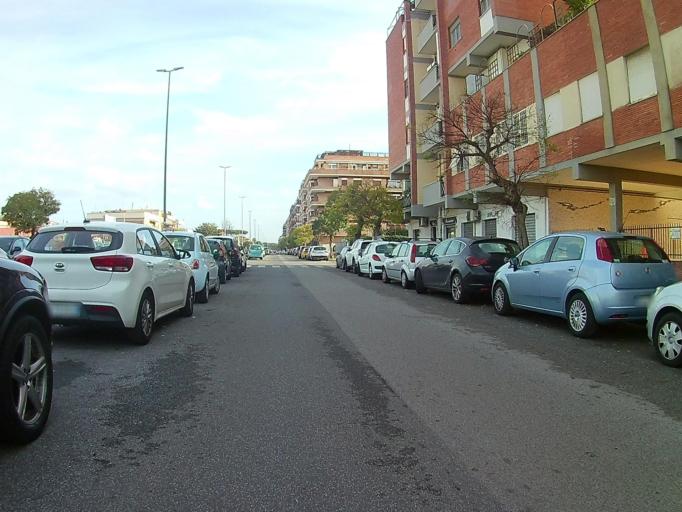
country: IT
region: Latium
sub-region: Citta metropolitana di Roma Capitale
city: Lido di Ostia
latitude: 41.7388
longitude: 12.2878
